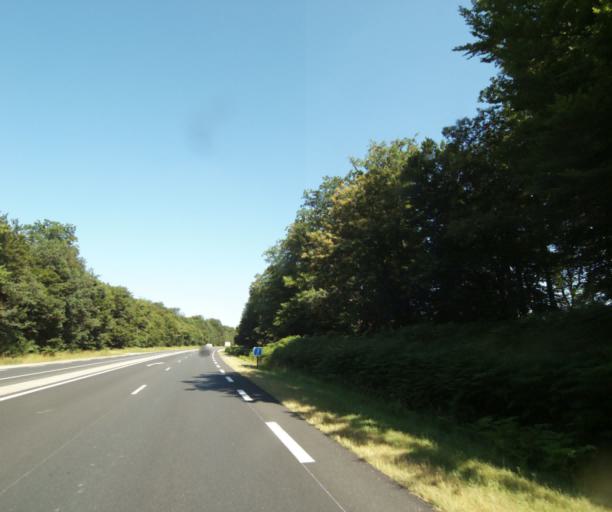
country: FR
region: Ile-de-France
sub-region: Departement de Seine-et-Marne
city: Avon
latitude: 48.3957
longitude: 2.7388
